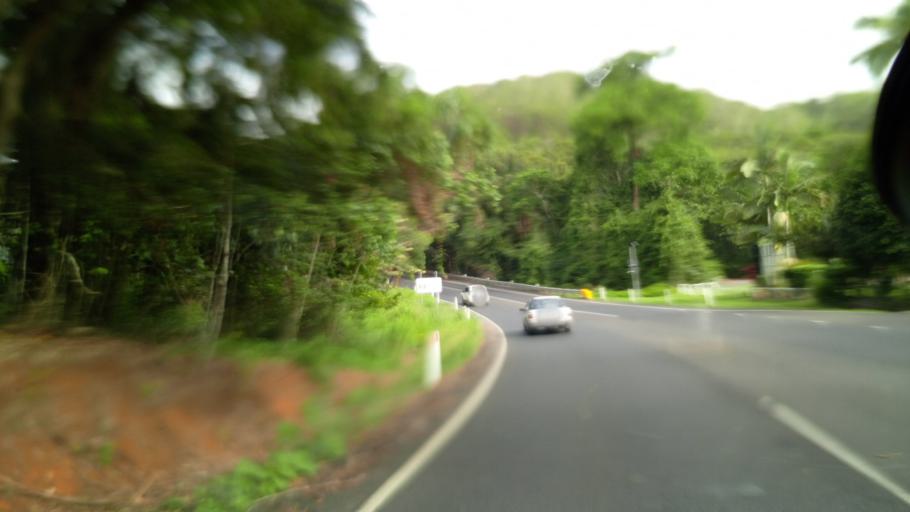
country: AU
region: Queensland
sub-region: Tablelands
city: Kuranda
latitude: -16.8244
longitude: 145.6512
